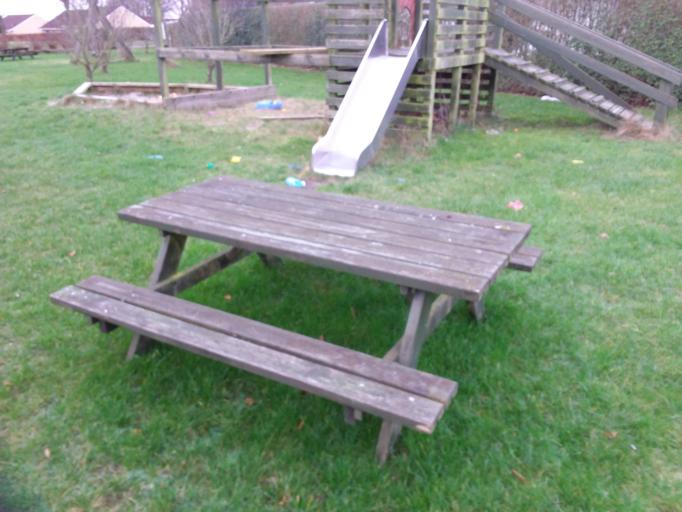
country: DK
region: Capital Region
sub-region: Frederikssund Kommune
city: Slangerup
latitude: 55.8551
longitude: 12.1804
